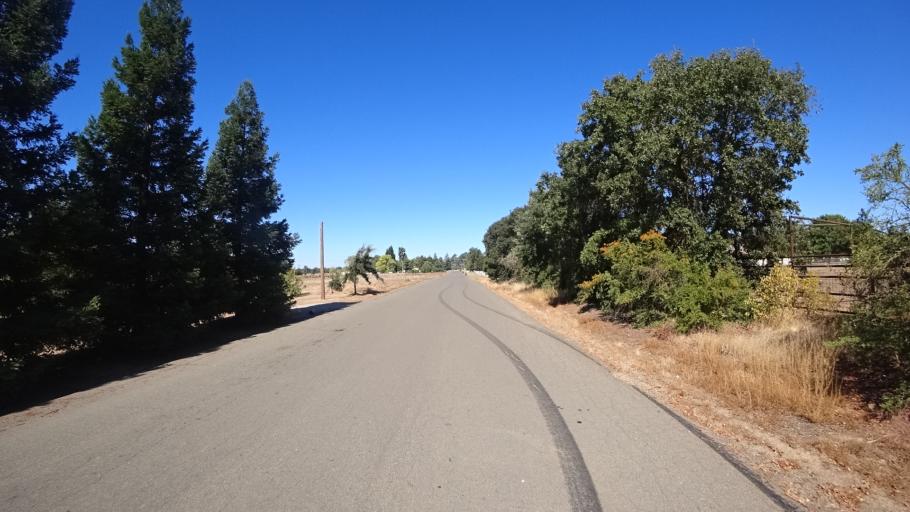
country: US
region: California
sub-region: Sacramento County
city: Wilton
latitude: 38.4206
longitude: -121.3063
